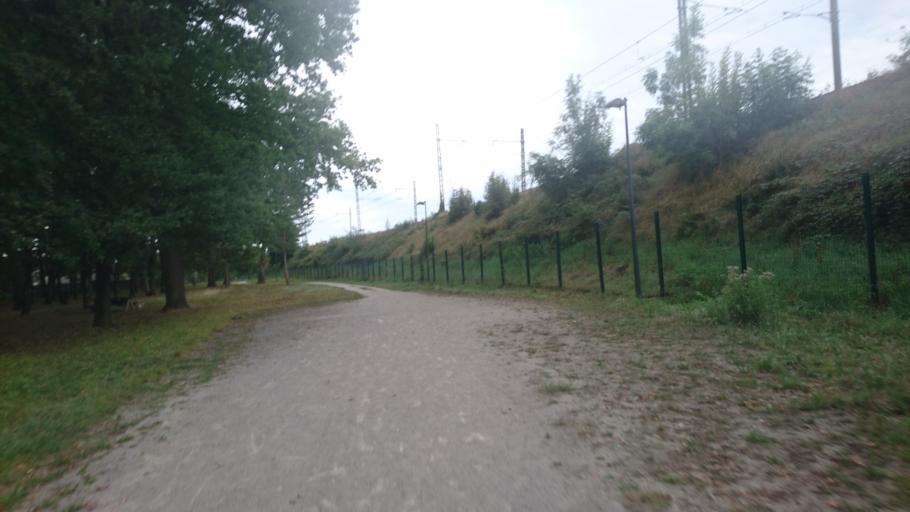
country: FR
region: Limousin
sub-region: Departement de la Correze
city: Brive-la-Gaillarde
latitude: 45.1539
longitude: 1.4901
